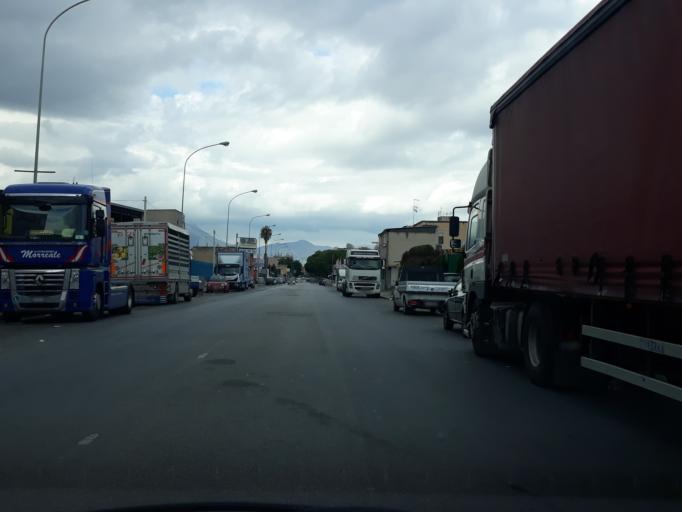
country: IT
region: Sicily
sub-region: Palermo
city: Ciaculli
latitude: 38.0943
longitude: 13.4018
